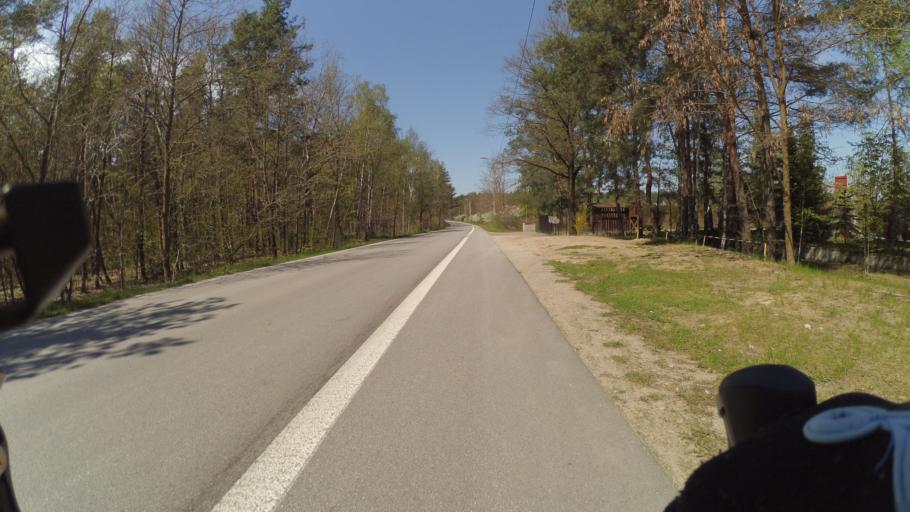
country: PL
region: Masovian Voivodeship
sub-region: Powiat nowodworski
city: Nowy Dwor Mazowiecki
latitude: 52.3910
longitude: 20.6795
